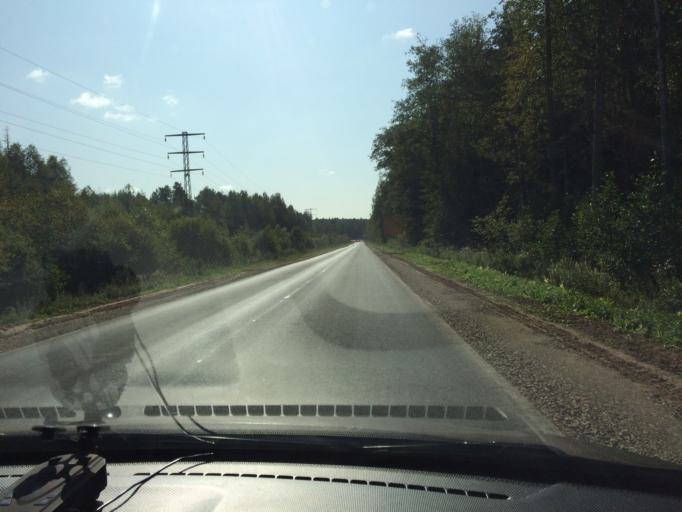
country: RU
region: Mariy-El
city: Surok
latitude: 56.5550
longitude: 48.3120
